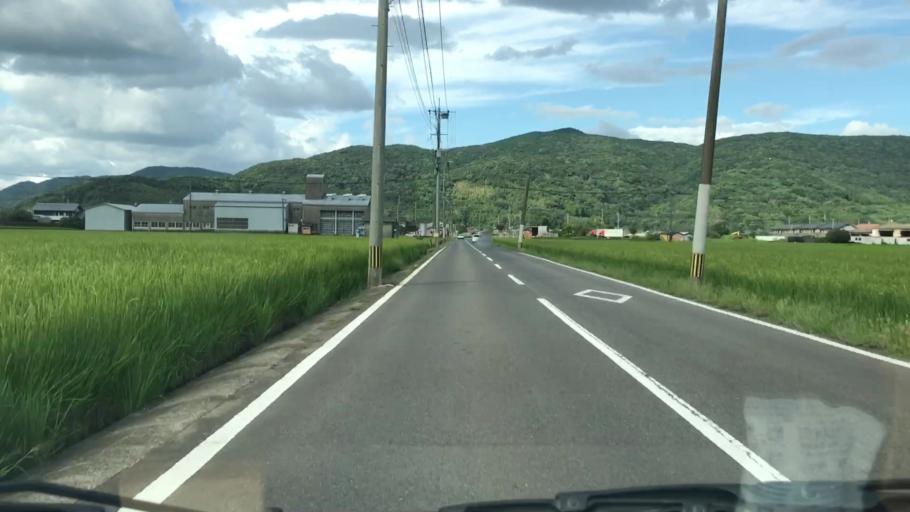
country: JP
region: Saga Prefecture
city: Kashima
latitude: 33.1212
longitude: 130.0717
